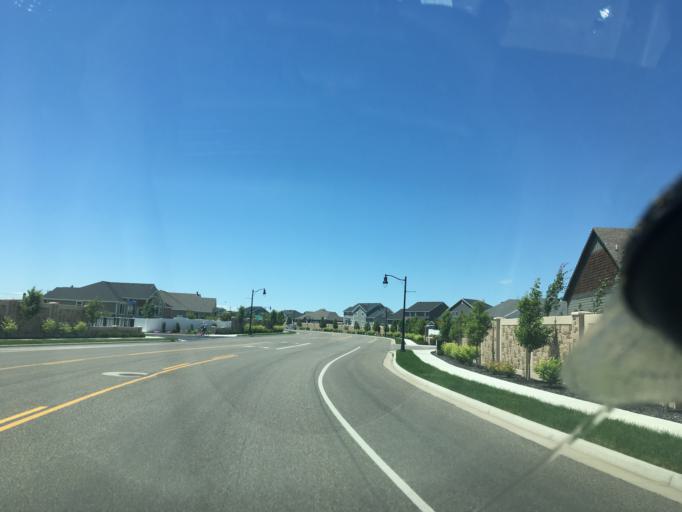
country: US
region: Utah
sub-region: Davis County
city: Layton
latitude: 41.0484
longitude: -111.9892
